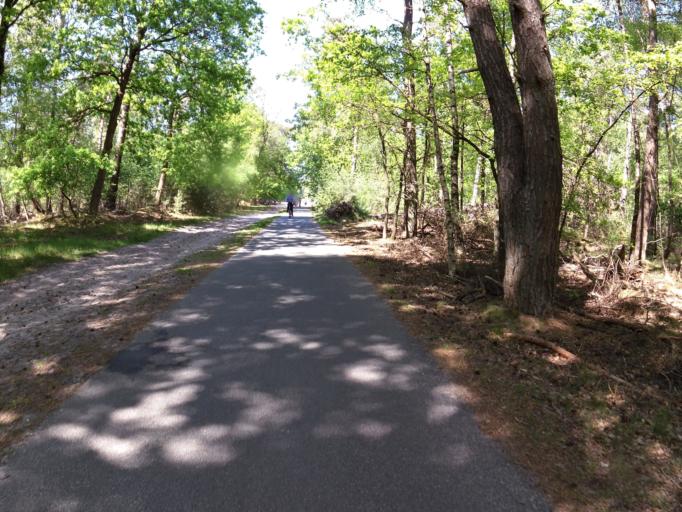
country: NL
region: North Brabant
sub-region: Gemeente Loon op Zand
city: Loon op Zand
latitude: 51.6485
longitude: 5.0719
